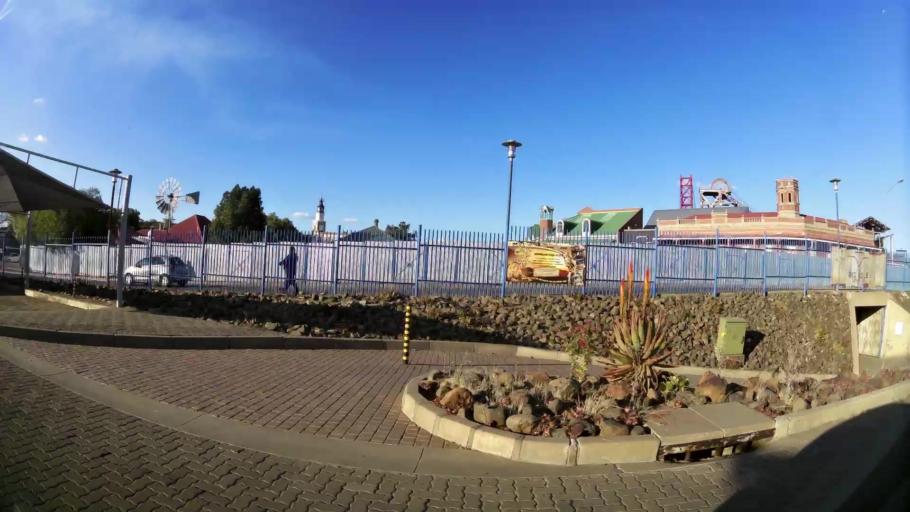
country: ZA
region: Northern Cape
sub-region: Frances Baard District Municipality
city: Kimberley
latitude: -28.7388
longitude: 24.7544
